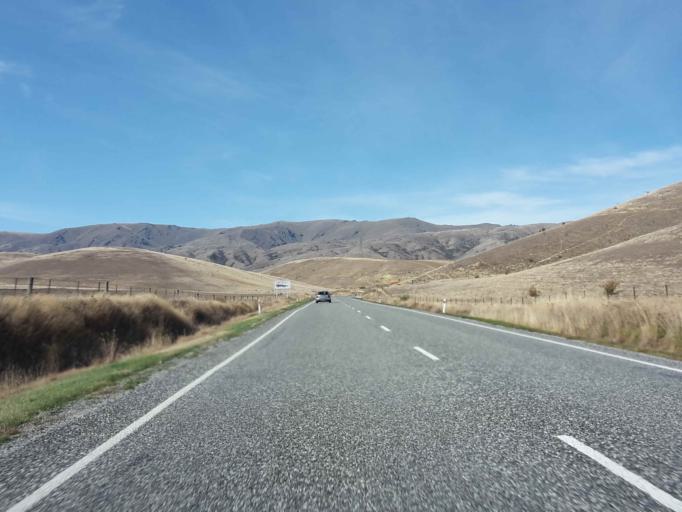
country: NZ
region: Otago
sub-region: Queenstown-Lakes District
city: Wanaka
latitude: -44.8049
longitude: 169.4819
